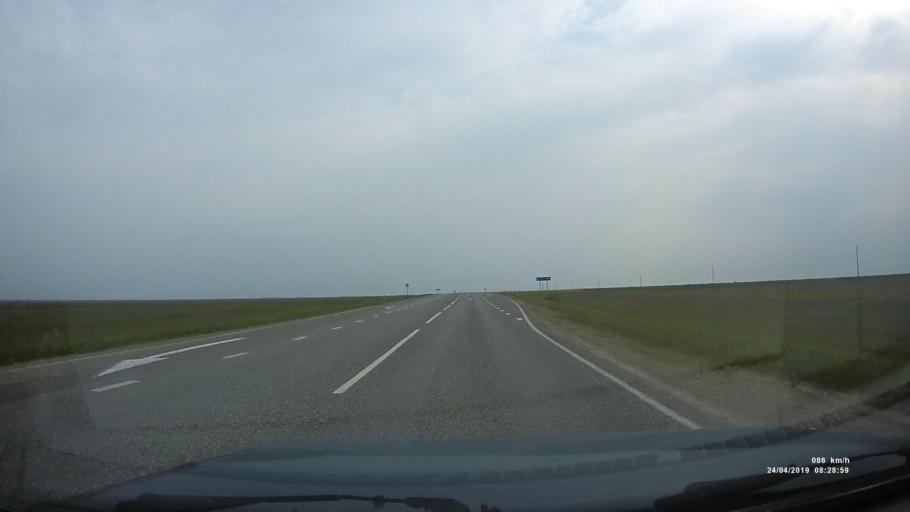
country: RU
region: Kalmykiya
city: Priyutnoye
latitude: 46.1487
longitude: 43.8241
